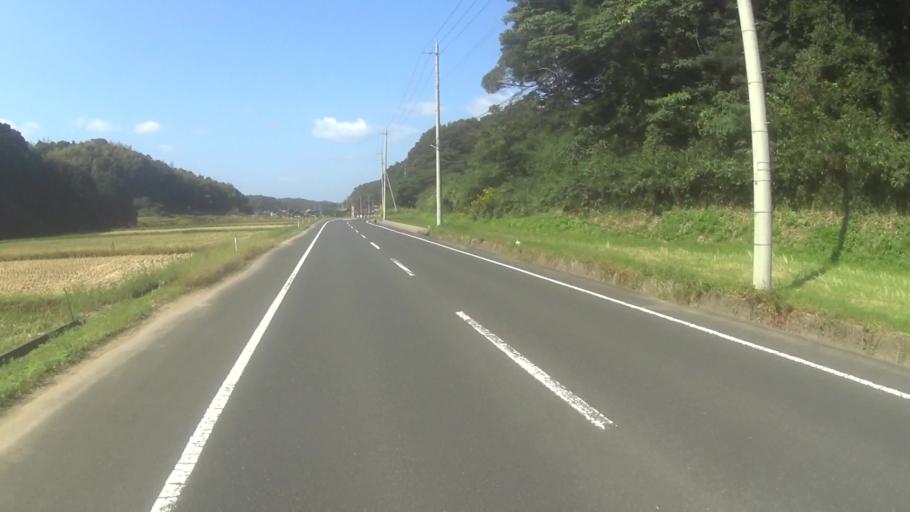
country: JP
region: Kyoto
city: Miyazu
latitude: 35.6722
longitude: 135.0564
